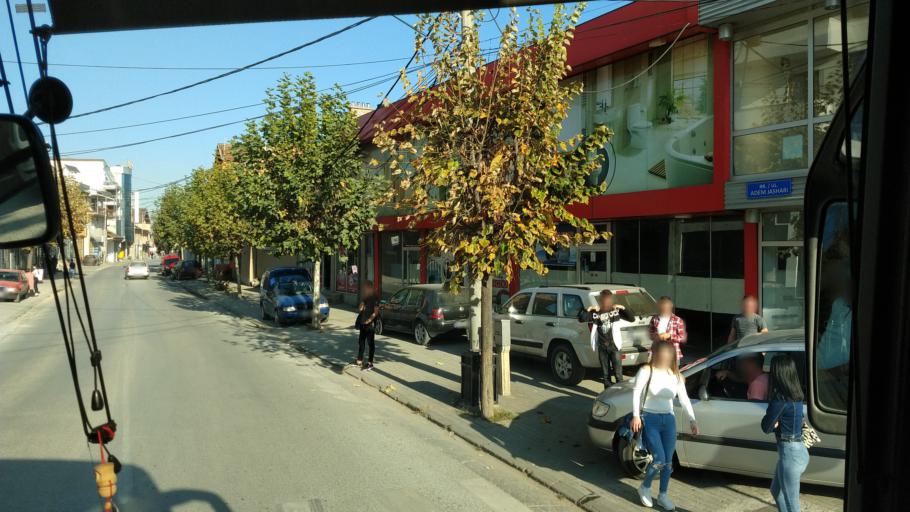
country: XK
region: Ferizaj
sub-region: Komuna e Shtimes
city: Shtime
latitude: 42.4330
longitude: 21.0403
